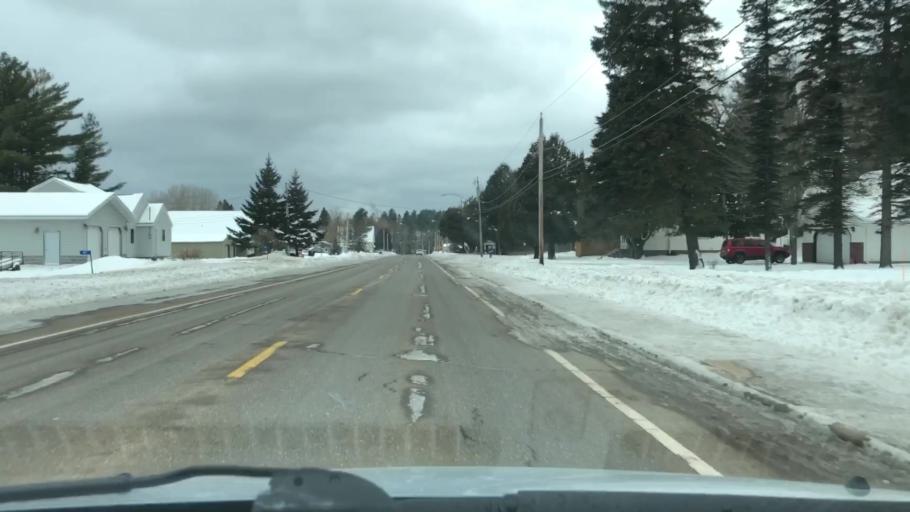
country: US
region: Minnesota
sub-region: Carlton County
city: Carlton
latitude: 46.6636
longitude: -92.3941
